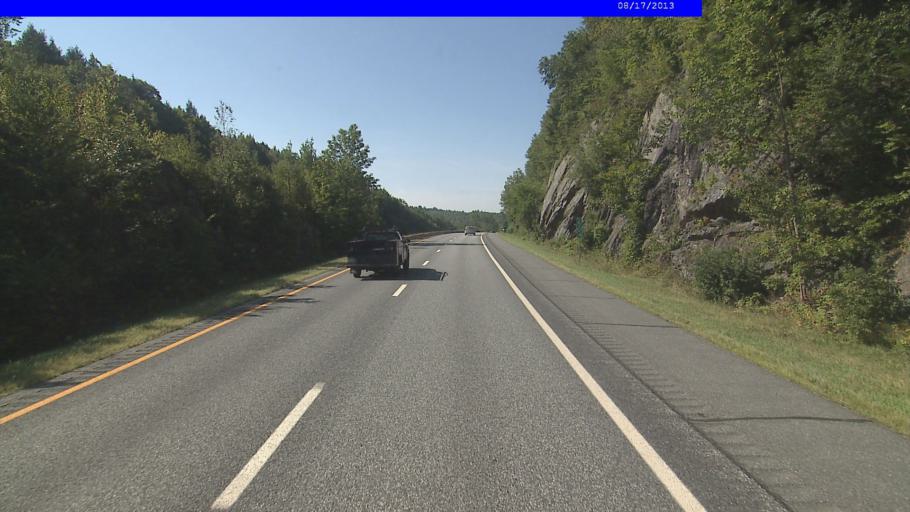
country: US
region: New Hampshire
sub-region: Sullivan County
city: Claremont
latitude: 43.3890
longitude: -72.4159
